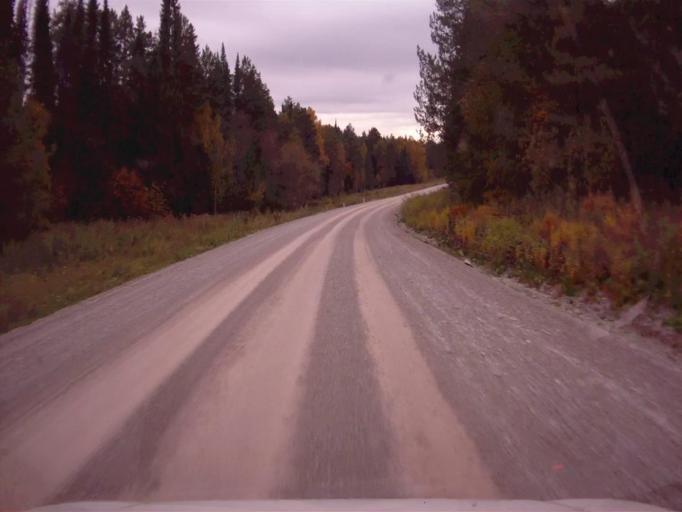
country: RU
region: Chelyabinsk
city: Nyazepetrovsk
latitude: 56.0489
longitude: 59.5289
